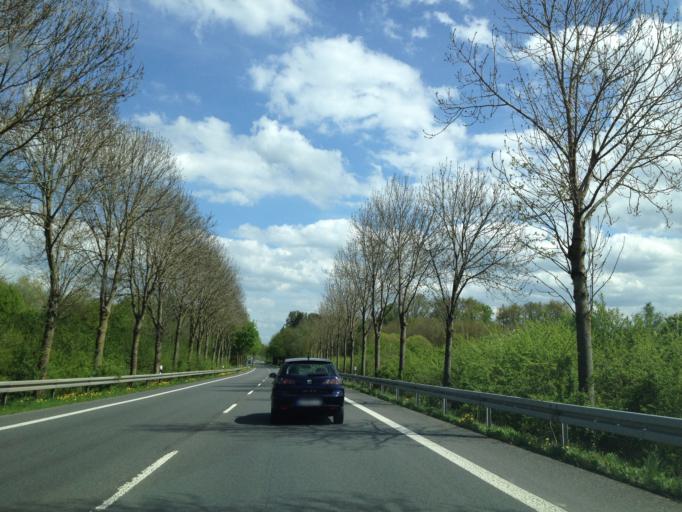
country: DE
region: North Rhine-Westphalia
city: Warstein
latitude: 51.4925
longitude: 8.3190
